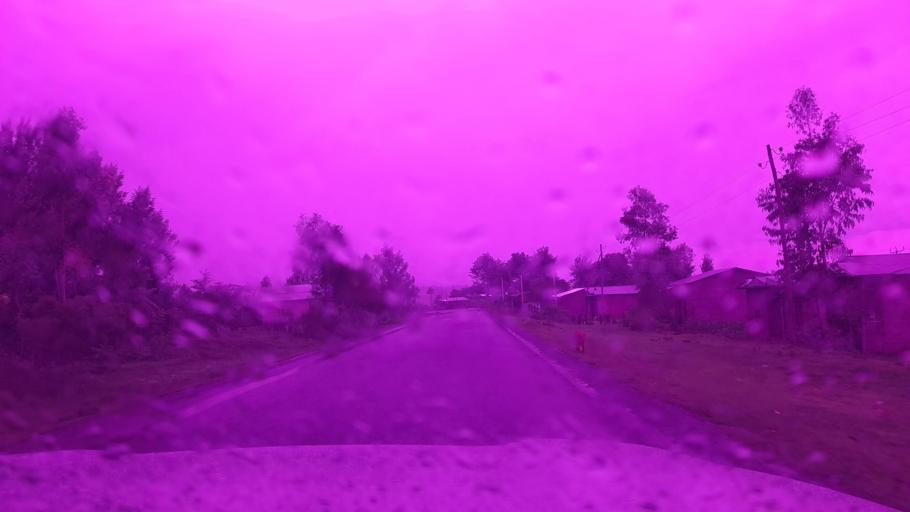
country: ET
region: Oromiya
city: Jima
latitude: 7.7183
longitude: 37.1045
